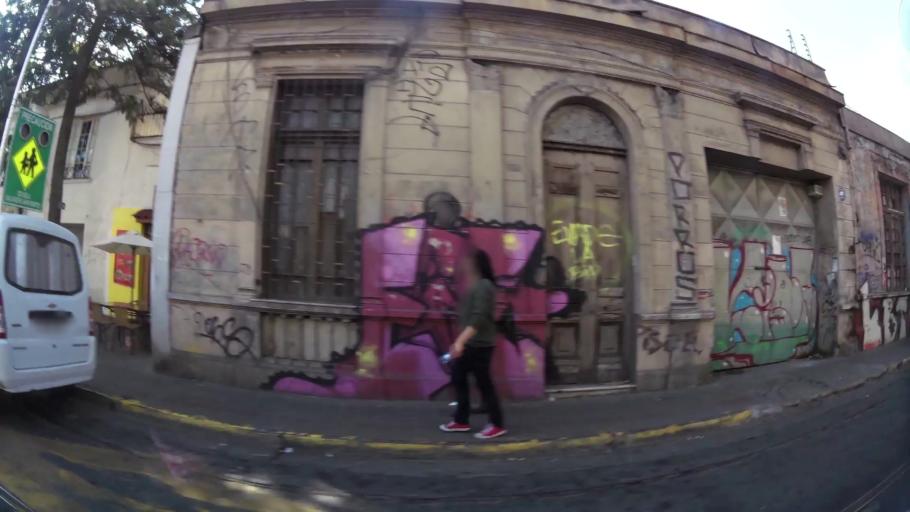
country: CL
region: Santiago Metropolitan
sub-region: Provincia de Santiago
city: Santiago
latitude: -33.4402
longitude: -70.6784
